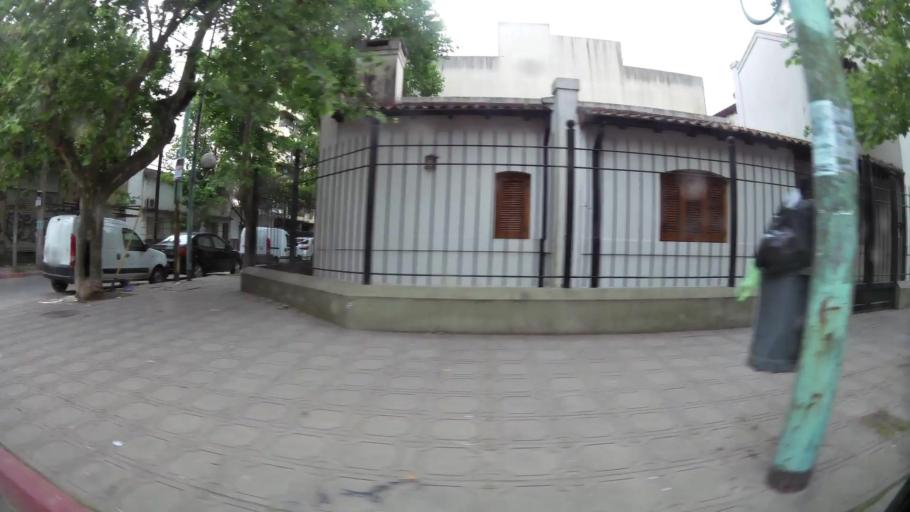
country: AR
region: Buenos Aires
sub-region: Partido de Zarate
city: Zarate
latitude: -34.0996
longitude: -59.0244
